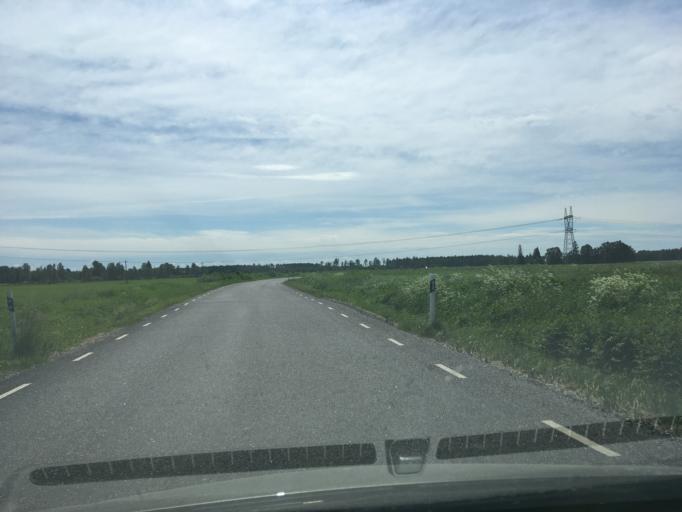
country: EE
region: Paernumaa
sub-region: Audru vald
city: Audru
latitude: 58.4366
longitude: 24.3984
